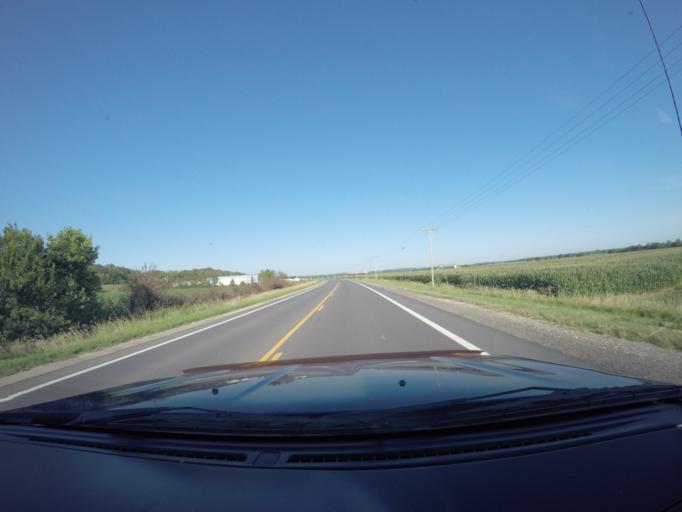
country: US
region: Kansas
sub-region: Douglas County
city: Lawrence
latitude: 39.0659
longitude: -95.3308
